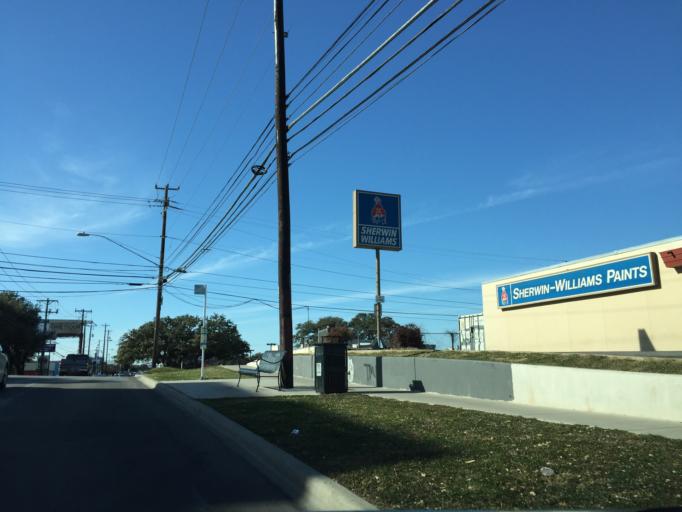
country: US
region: Texas
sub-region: Travis County
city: Austin
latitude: 30.2374
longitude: -97.7511
